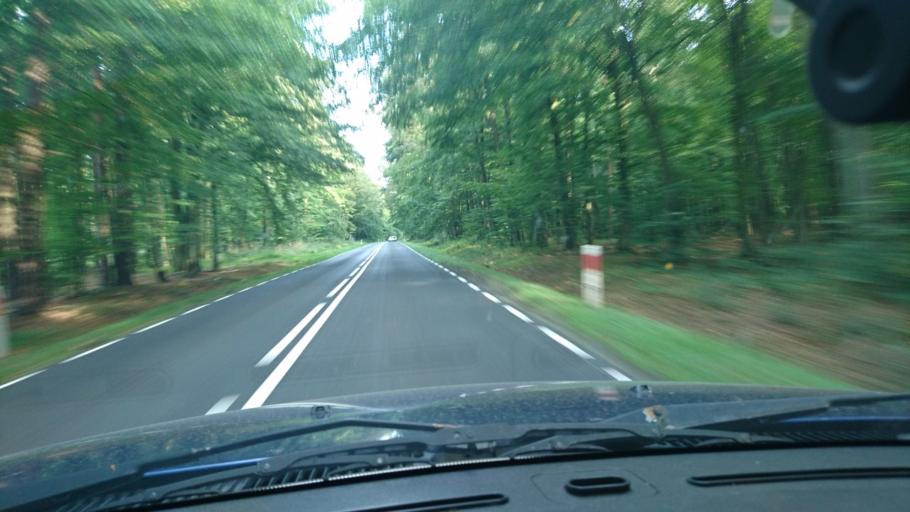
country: PL
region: Greater Poland Voivodeship
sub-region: Powiat krotoszynski
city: Krotoszyn
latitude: 51.6581
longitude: 17.4740
